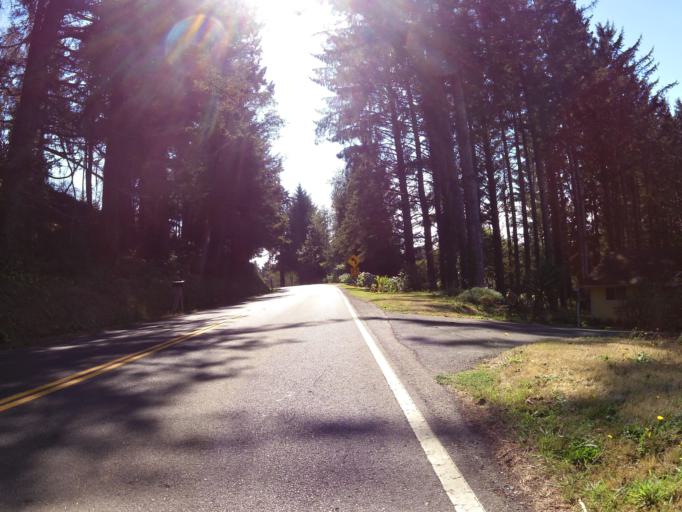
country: US
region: Oregon
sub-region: Curry County
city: Harbor
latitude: 41.9552
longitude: -124.2017
